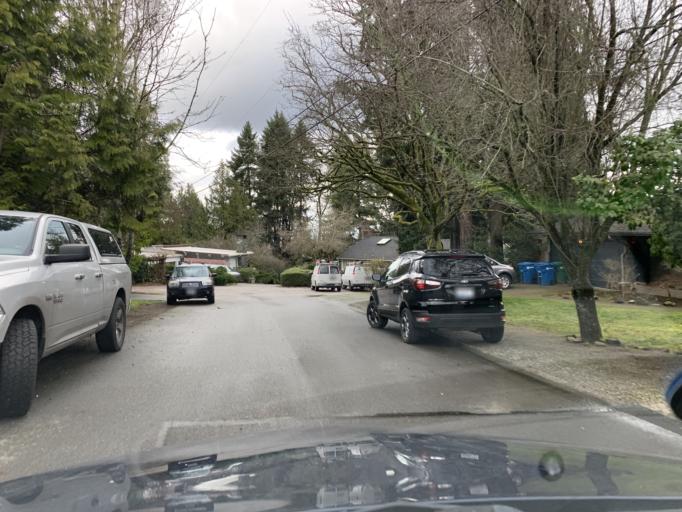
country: US
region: Washington
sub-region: King County
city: Mercer Island
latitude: 47.5848
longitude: -122.2412
